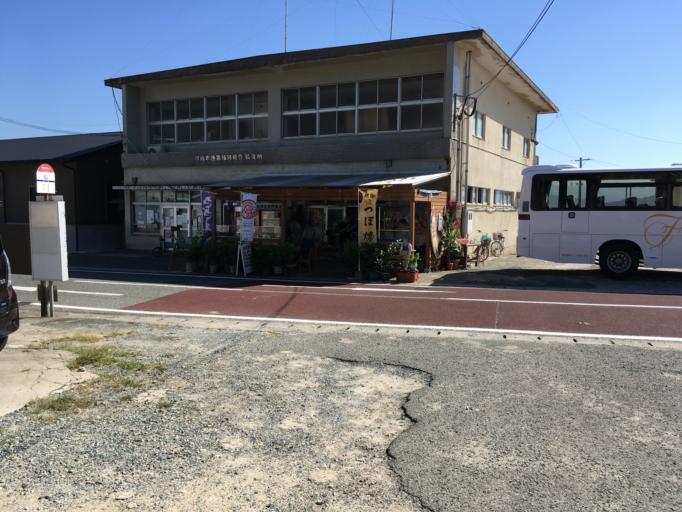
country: JP
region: Fukuoka
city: Fukuoka-shi
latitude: 33.6710
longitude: 130.2912
